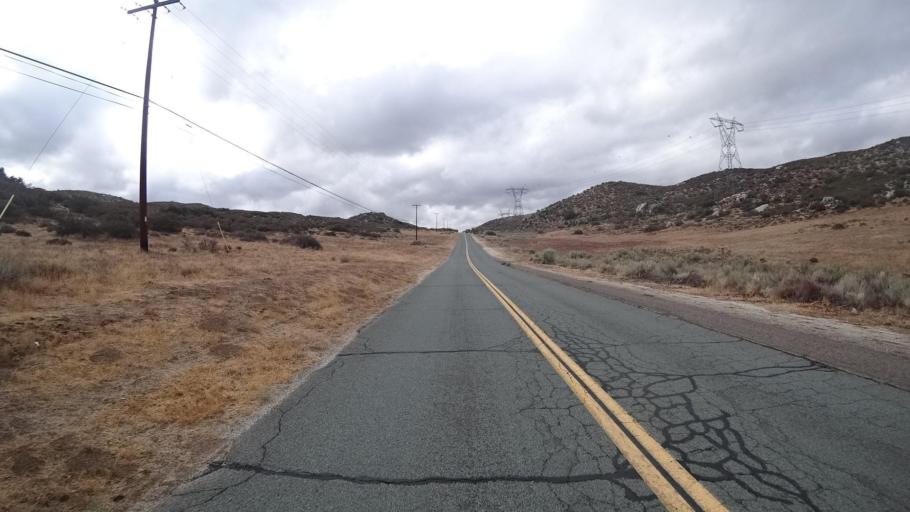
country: US
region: California
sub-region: San Diego County
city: Campo
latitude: 32.7148
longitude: -116.4300
